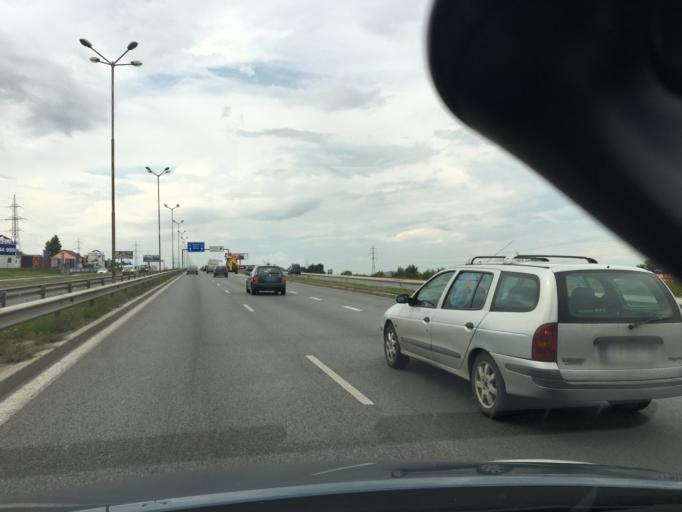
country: BG
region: Sofia-Capital
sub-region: Stolichna Obshtina
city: Sofia
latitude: 42.6260
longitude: 23.3509
